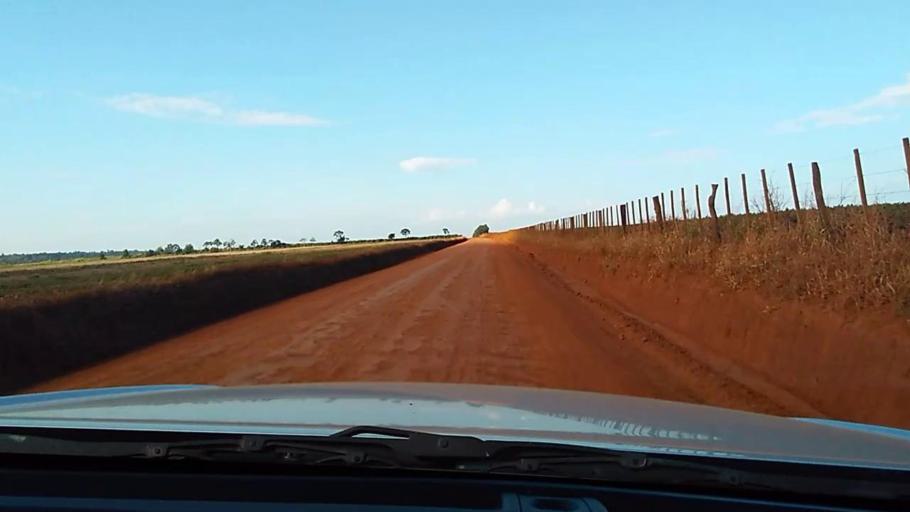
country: PY
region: Alto Parana
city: Naranjal
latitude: -25.7103
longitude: -55.3907
